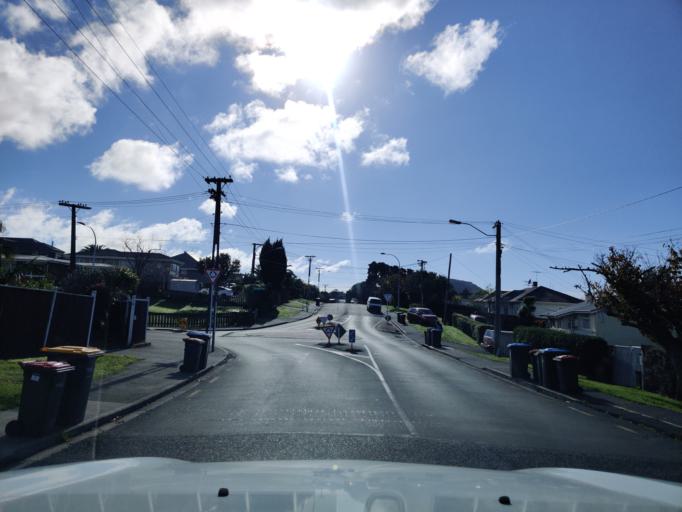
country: NZ
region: Auckland
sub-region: Auckland
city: Tamaki
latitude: -36.9043
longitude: 174.8361
